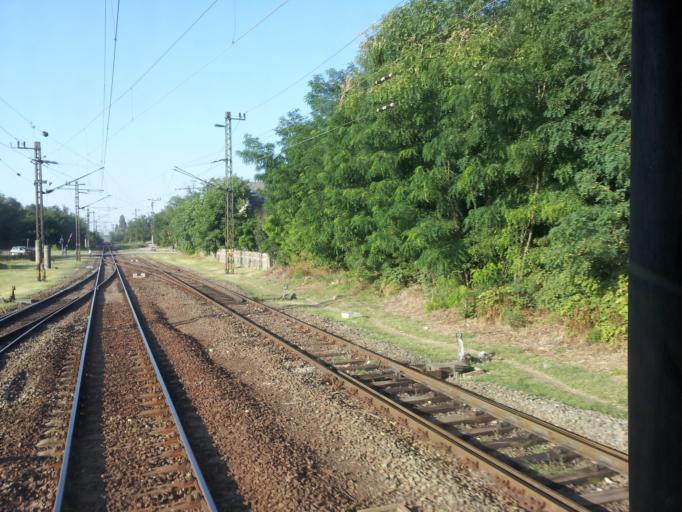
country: HU
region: Pest
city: Taksony
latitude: 47.3172
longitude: 19.0761
